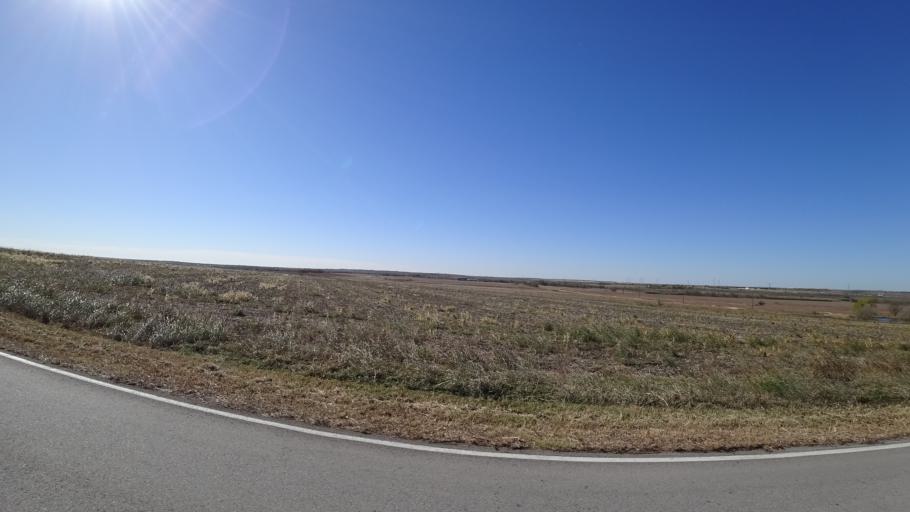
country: US
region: Texas
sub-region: Travis County
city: Garfield
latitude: 30.1051
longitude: -97.6437
